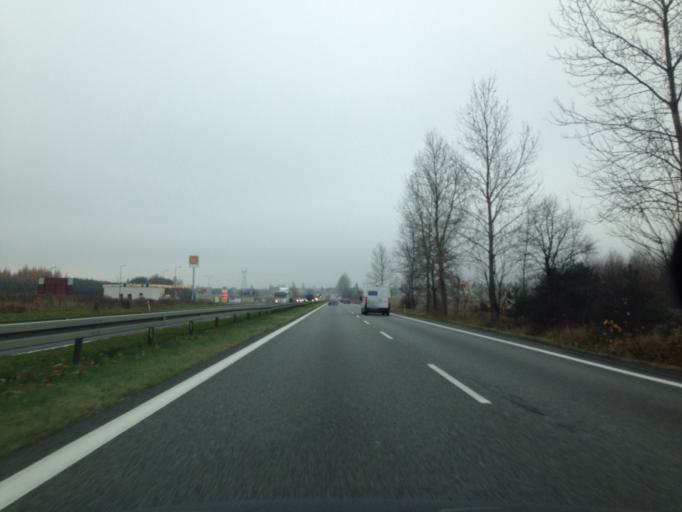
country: PL
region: Silesian Voivodeship
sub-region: Powiat bedzinski
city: Siewierz
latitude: 50.5146
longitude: 19.1947
